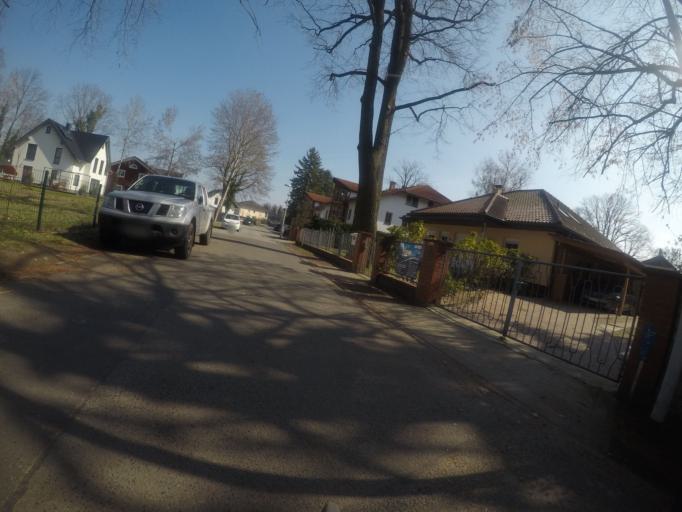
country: DE
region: Brandenburg
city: Konigs Wusterhausen
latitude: 52.2927
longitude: 13.6808
